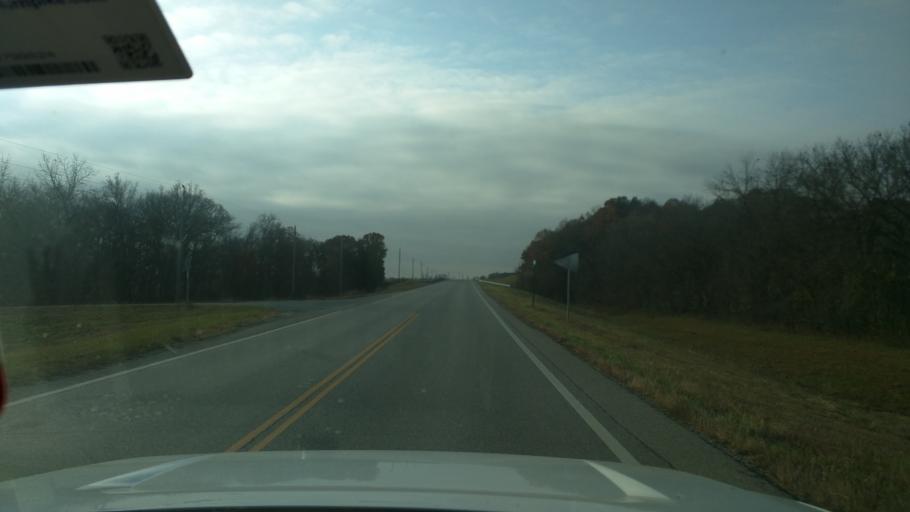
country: US
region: Kansas
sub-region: Greenwood County
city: Eureka
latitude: 37.7410
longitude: -96.2296
